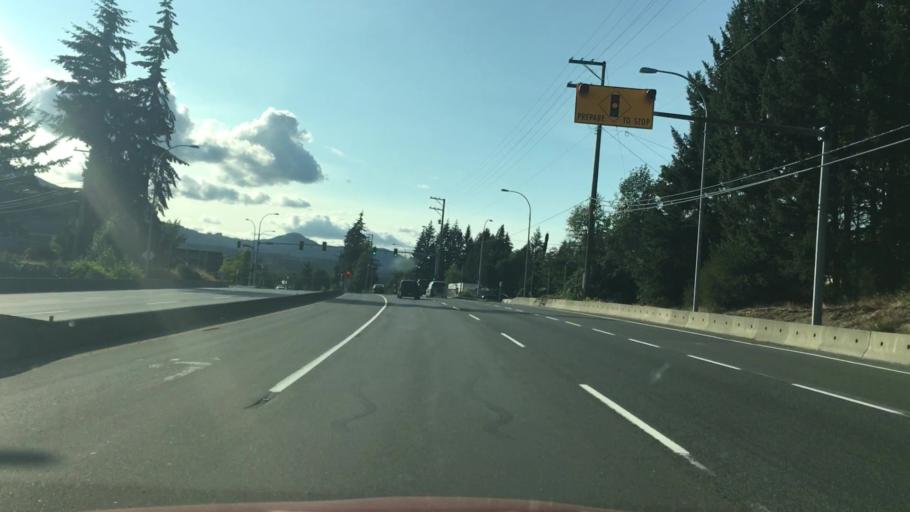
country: CA
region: British Columbia
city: North Cowichan
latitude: 48.9069
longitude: -123.7270
